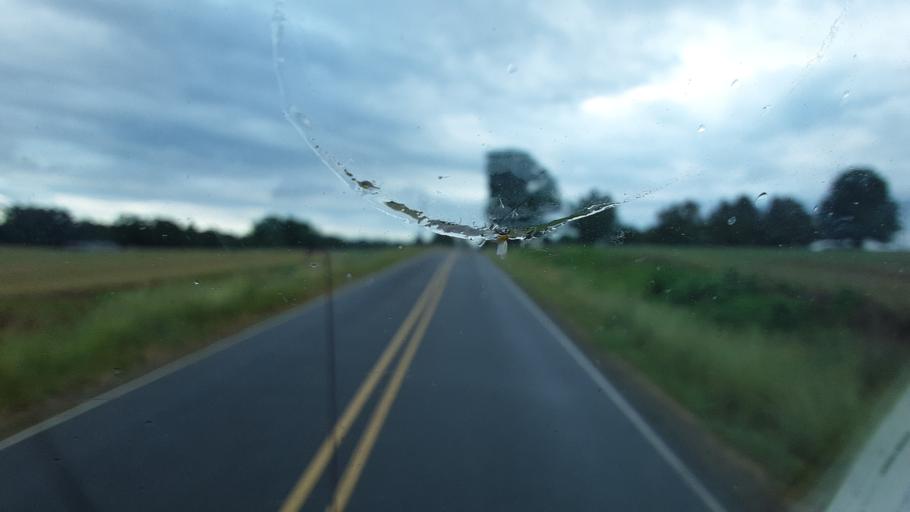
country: US
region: North Carolina
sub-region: Yadkin County
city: Jonesville
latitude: 36.0584
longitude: -80.8311
